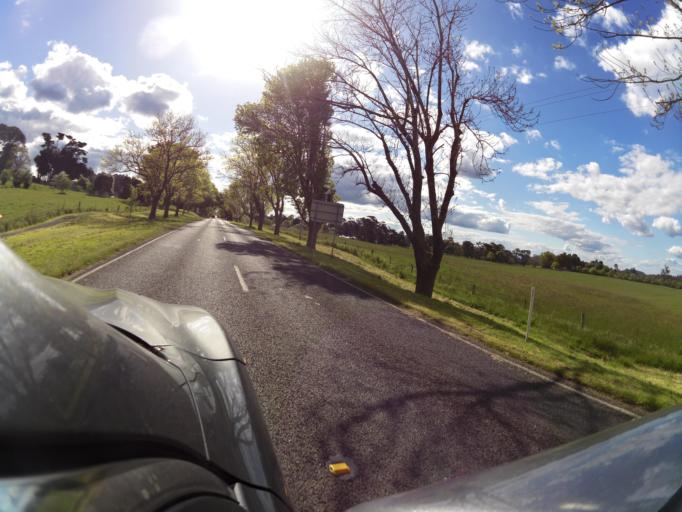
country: AU
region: Victoria
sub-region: Mount Alexander
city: Castlemaine
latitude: -37.3415
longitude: 144.1627
